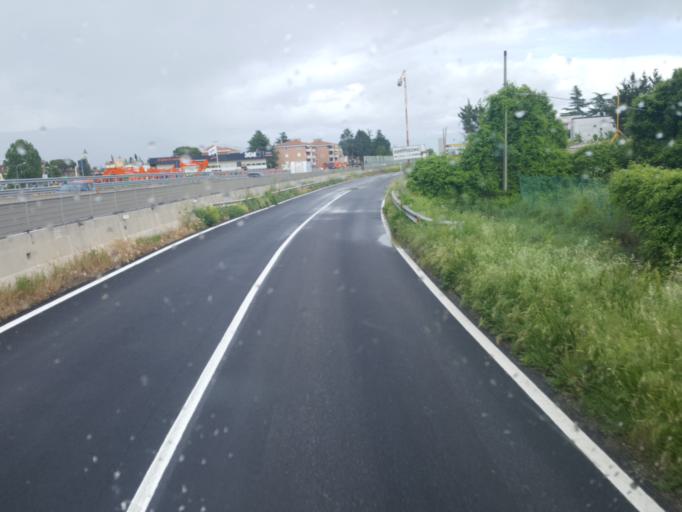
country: IT
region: Umbria
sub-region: Provincia di Perugia
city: Ospedalicchio
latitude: 43.0805
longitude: 12.4971
